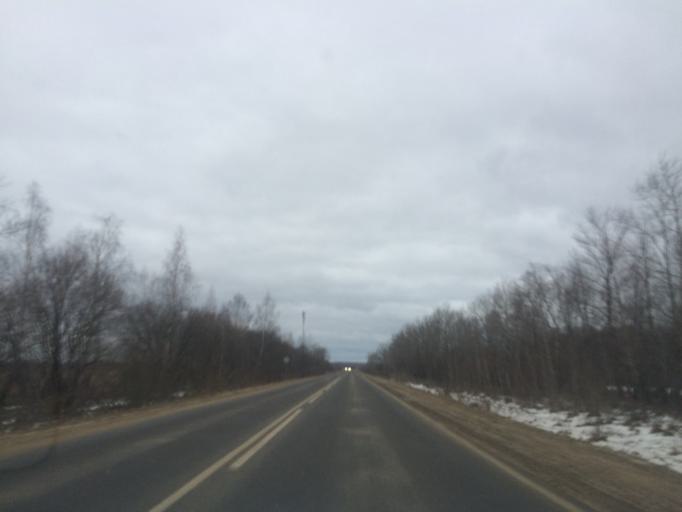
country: RU
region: Tula
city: Odoyev
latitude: 53.9949
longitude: 36.7491
